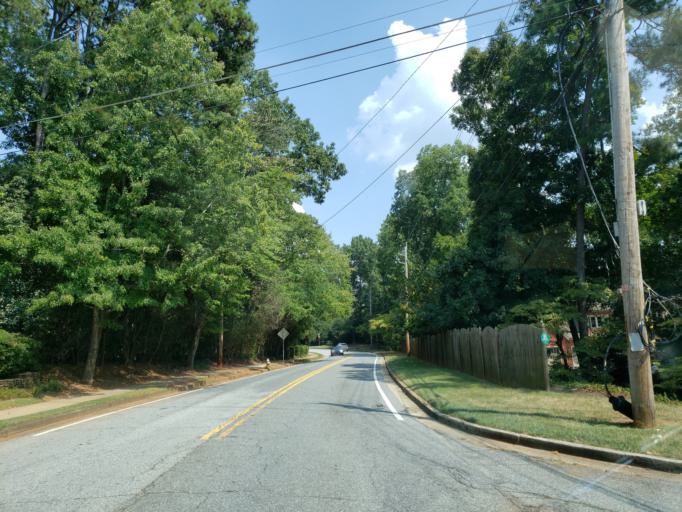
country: US
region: Georgia
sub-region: Fulton County
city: Sandy Springs
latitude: 33.9001
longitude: -84.4231
